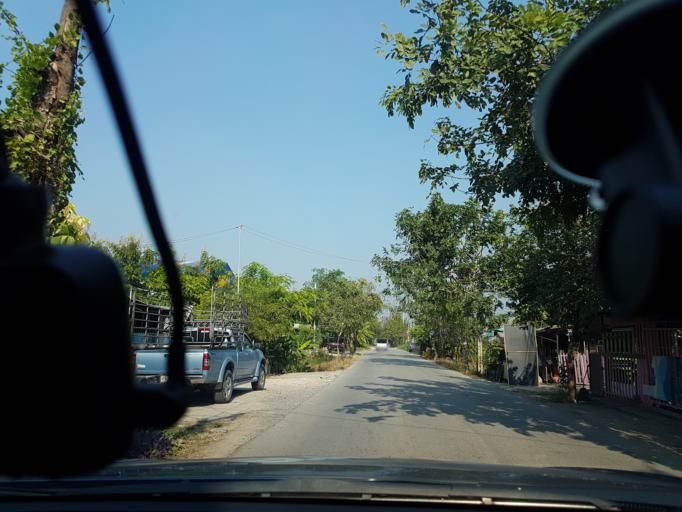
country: TH
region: Pathum Thani
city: Lam Luk Ka
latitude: 13.9064
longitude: 100.6998
